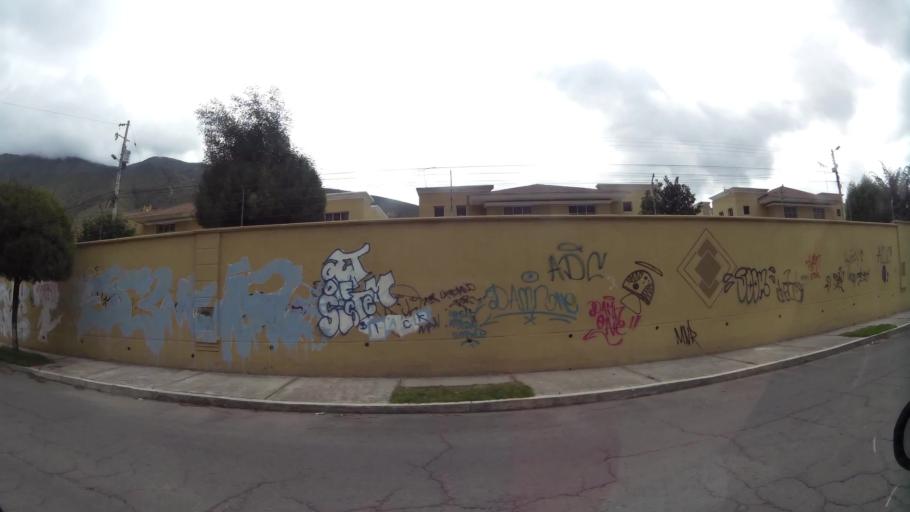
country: EC
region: Pichincha
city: Quito
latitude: -0.0154
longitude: -78.4507
